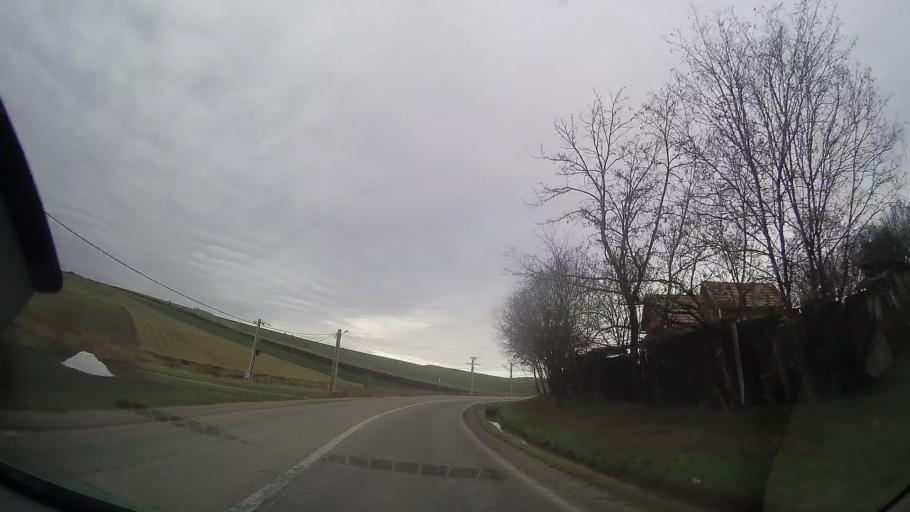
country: RO
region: Cluj
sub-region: Comuna Camarasu
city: Camarasu
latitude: 46.7981
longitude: 24.1660
